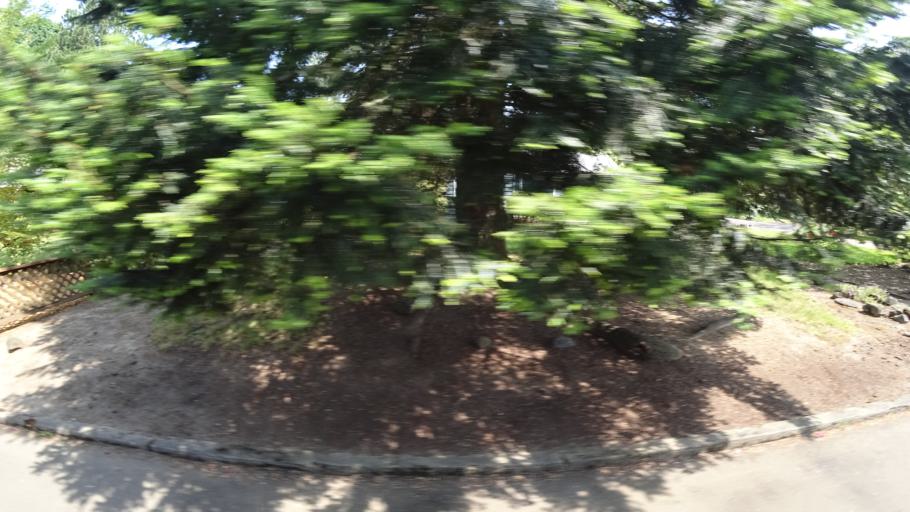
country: US
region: Oregon
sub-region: Washington County
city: Cedar Mill
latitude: 45.5200
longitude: -122.8182
